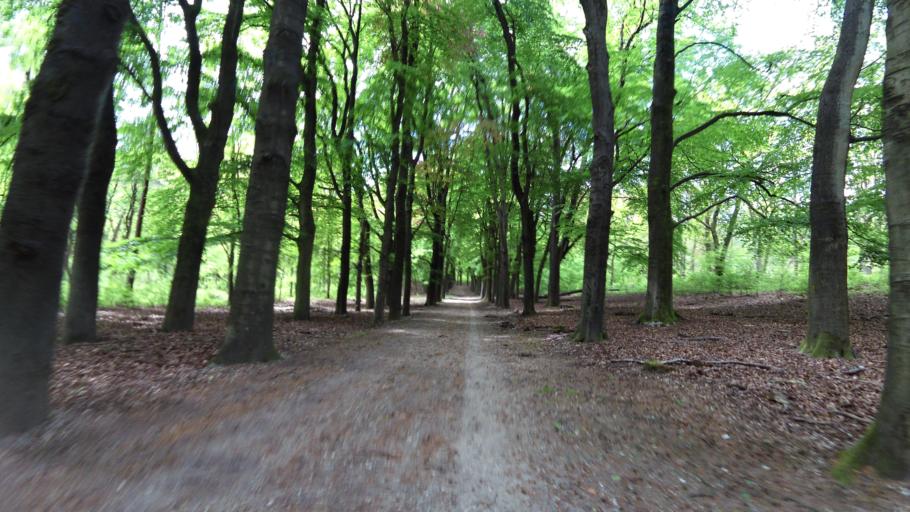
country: NL
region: Gelderland
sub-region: Gemeente Rheden
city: De Steeg
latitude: 52.0455
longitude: 6.0360
